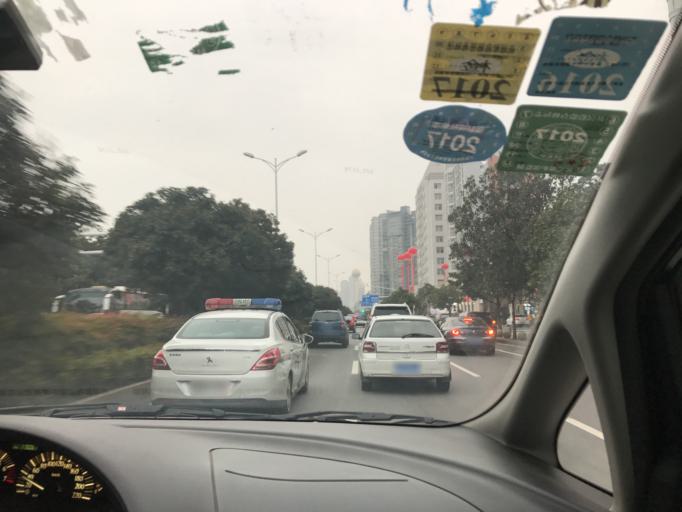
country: CN
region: Hubei
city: Jiang'an
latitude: 30.6081
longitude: 114.3080
